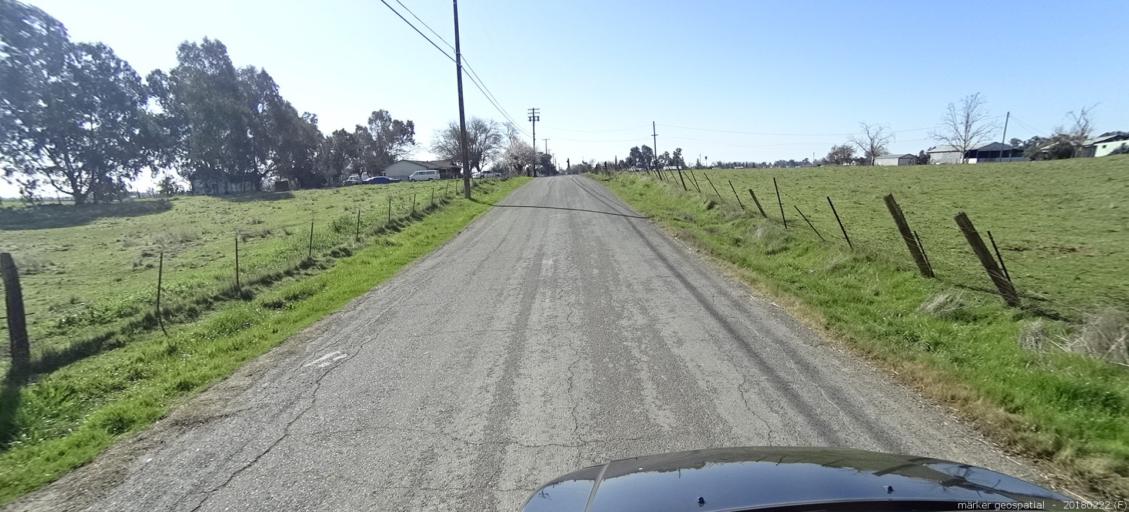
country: US
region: California
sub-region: Sacramento County
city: Elverta
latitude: 38.7249
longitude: -121.4435
